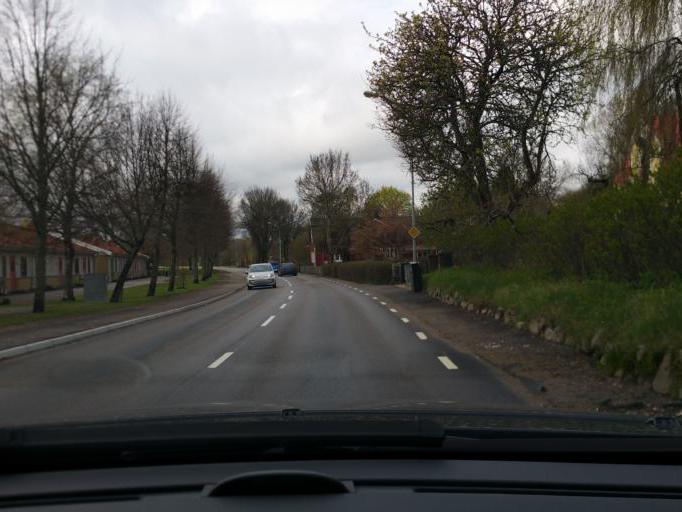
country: SE
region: Kronoberg
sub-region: Vaxjo Kommun
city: Ingelstad
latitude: 56.7419
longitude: 14.9268
